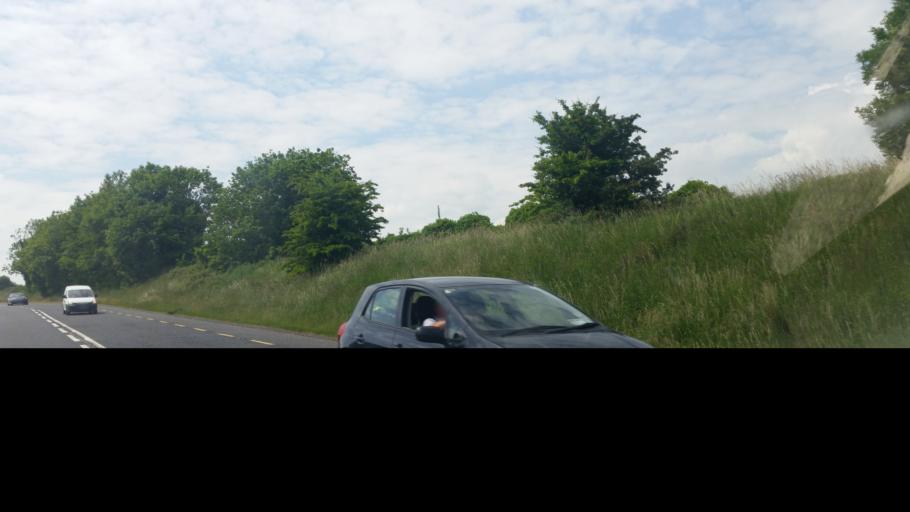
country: IE
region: Leinster
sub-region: An Mhi
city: Slane
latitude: 53.7076
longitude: -6.5714
